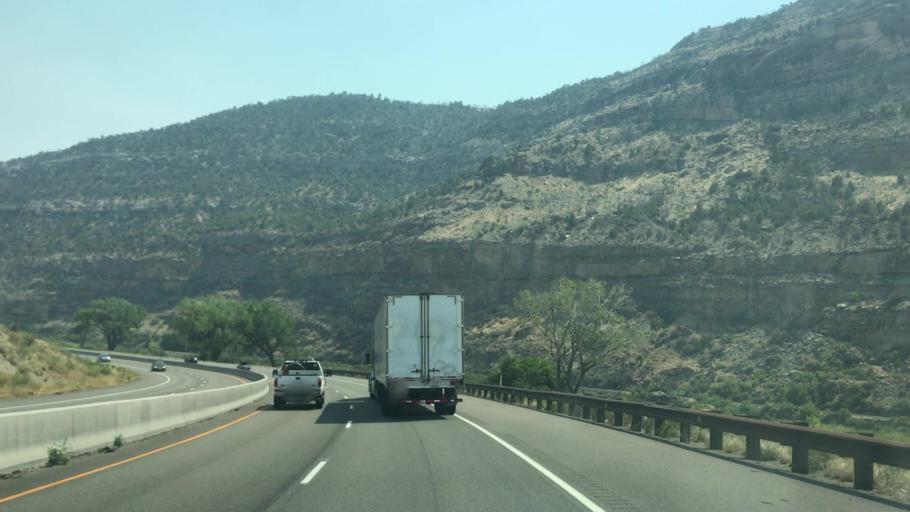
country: US
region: Colorado
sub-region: Mesa County
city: Palisade
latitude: 39.2329
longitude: -108.2724
